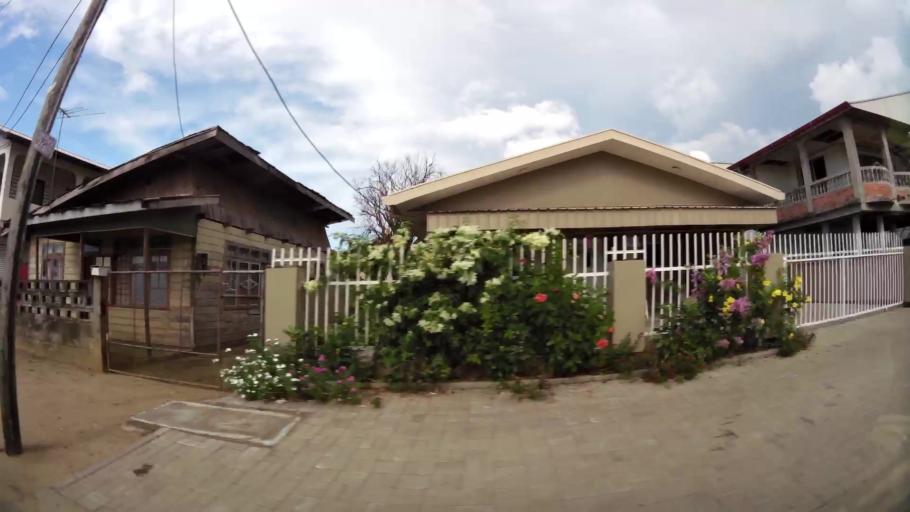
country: SR
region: Paramaribo
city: Paramaribo
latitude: 5.8523
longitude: -55.1834
